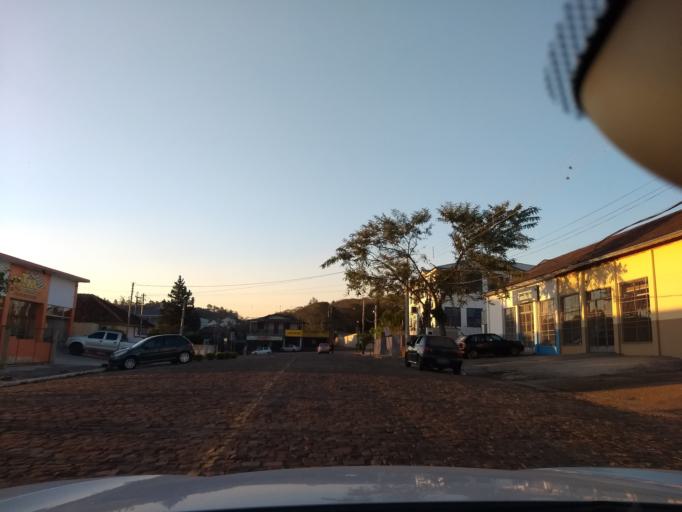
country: BR
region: Rio Grande do Sul
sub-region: Santa Cruz Do Sul
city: Santa Cruz do Sul
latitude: -29.7162
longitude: -52.5064
